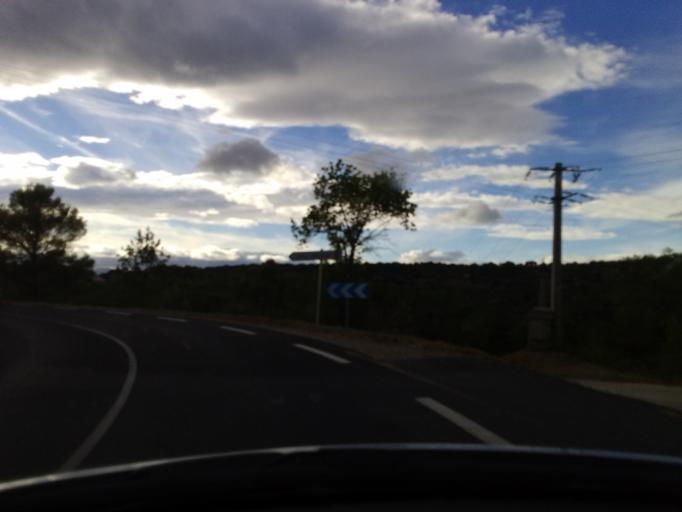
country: FR
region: Languedoc-Roussillon
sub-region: Departement de l'Herault
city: Nebian
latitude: 43.6406
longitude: 3.4173
